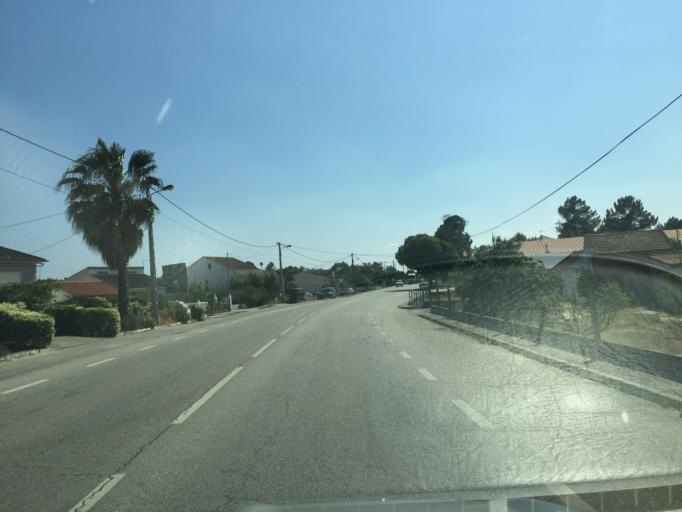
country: PT
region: Santarem
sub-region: Chamusca
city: Vila Nova da Barquinha
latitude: 39.4140
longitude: -8.4221
